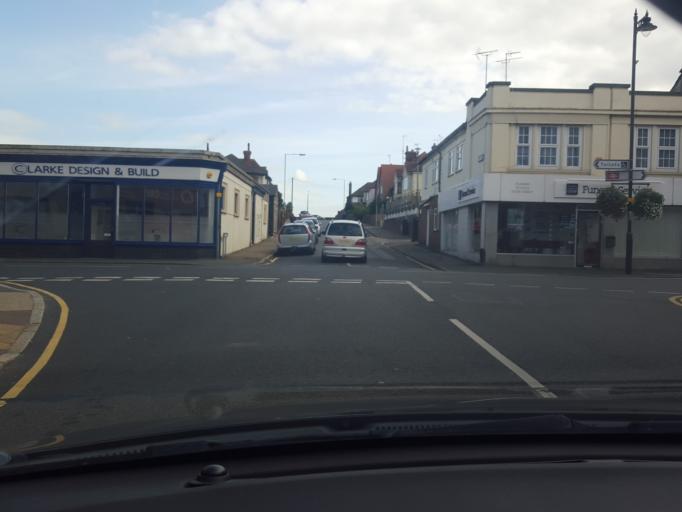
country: GB
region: England
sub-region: Essex
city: Dovercourt
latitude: 51.9377
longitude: 1.2816
